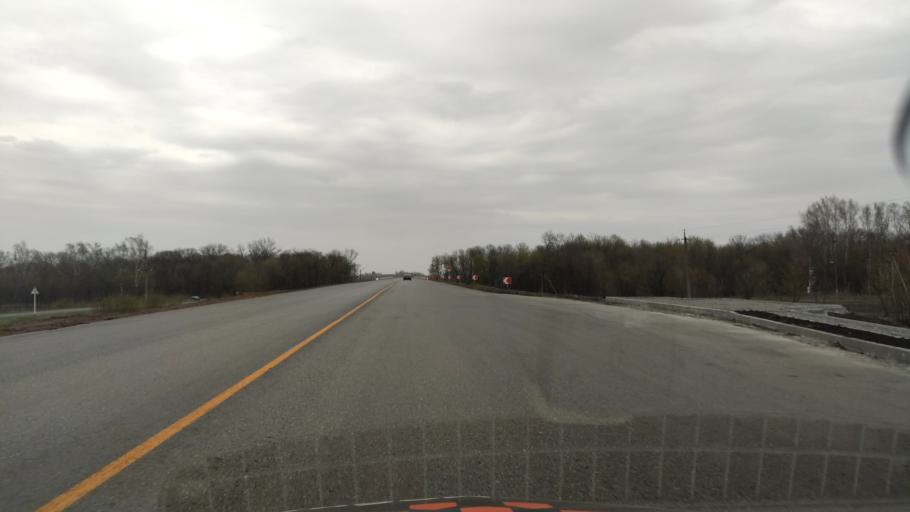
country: RU
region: Kursk
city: Gorshechnoye
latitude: 51.5529
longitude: 38.0344
